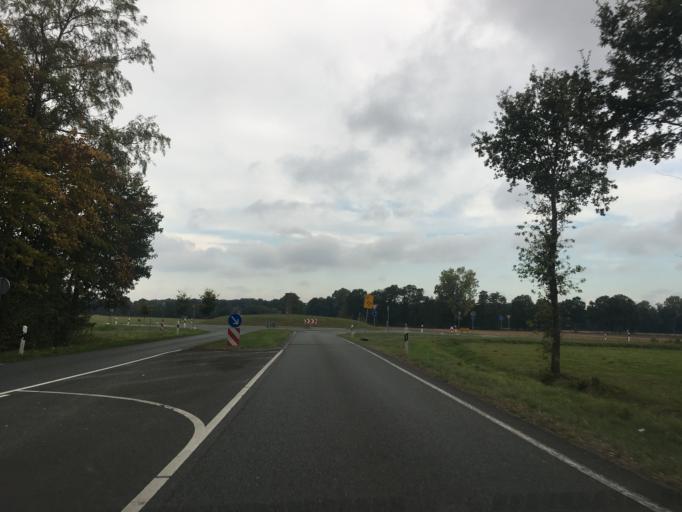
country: DE
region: North Rhine-Westphalia
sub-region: Regierungsbezirk Munster
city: Schoppingen
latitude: 52.1035
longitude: 7.2013
